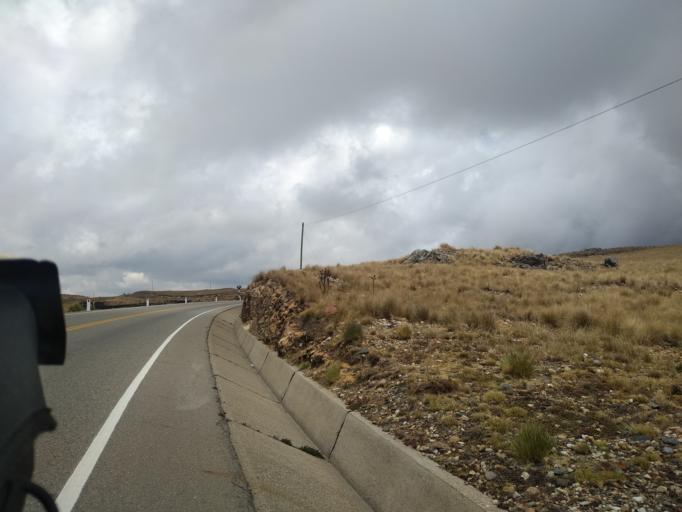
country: PE
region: La Libertad
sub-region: Provincia de Santiago de Chuco
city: Quiruvilca
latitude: -7.9541
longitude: -78.1925
